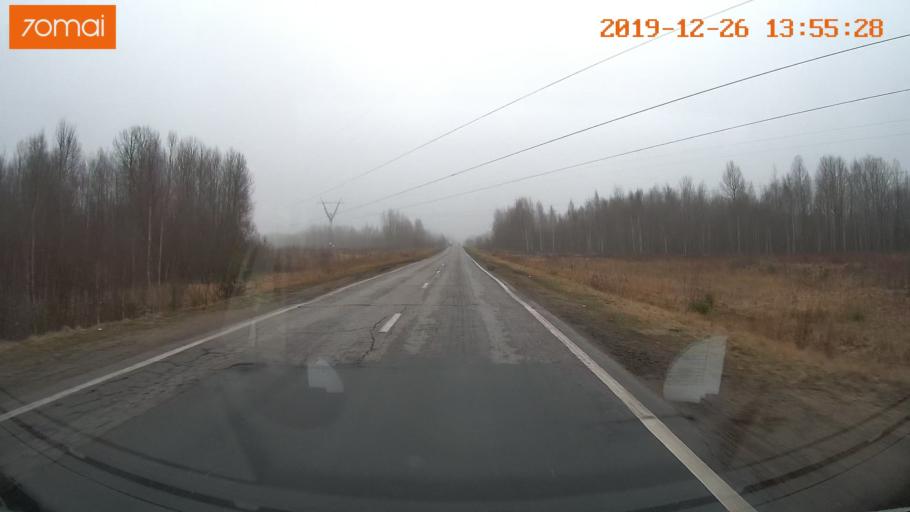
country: RU
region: Jaroslavl
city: Poshekhon'ye
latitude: 58.6031
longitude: 38.6475
